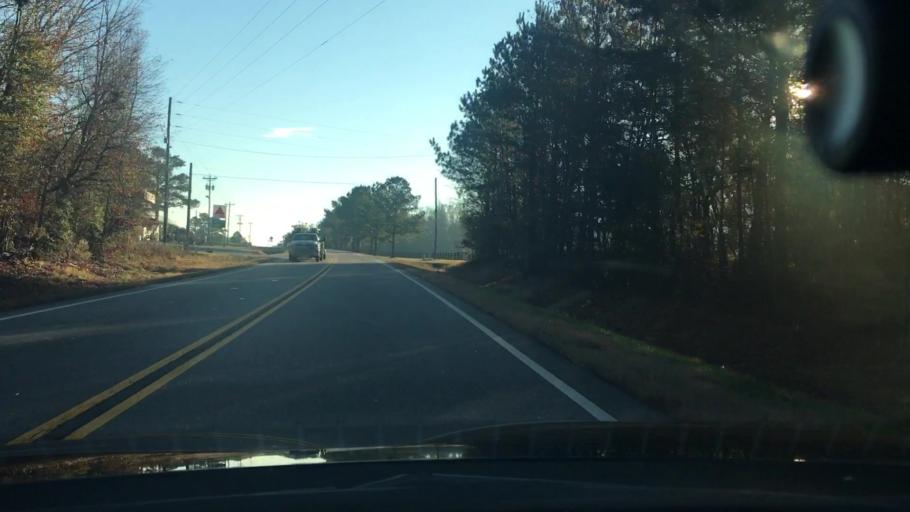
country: US
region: Georgia
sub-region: Coweta County
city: Senoia
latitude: 33.2502
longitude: -84.4711
